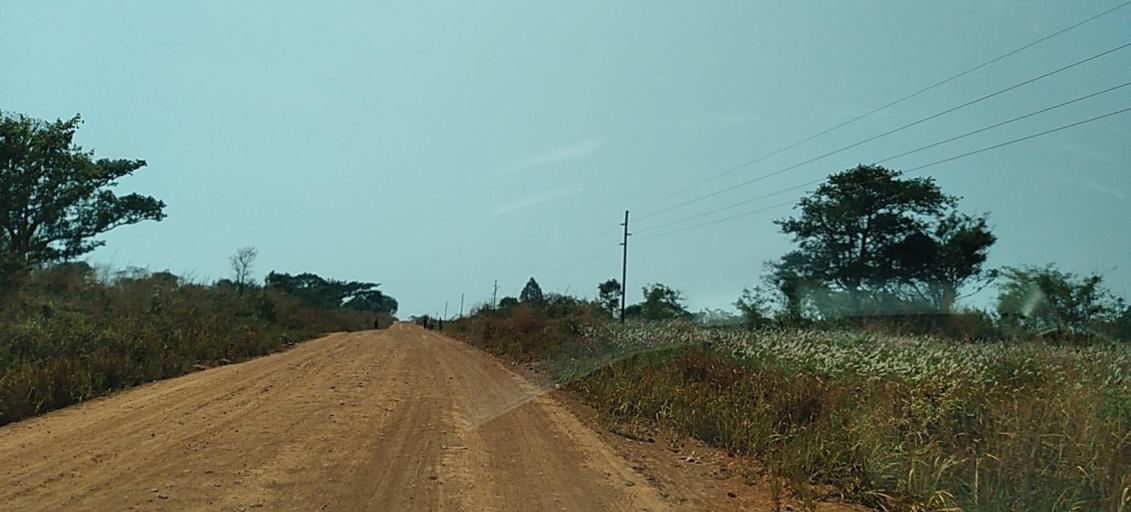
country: ZM
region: North-Western
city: Kansanshi
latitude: -12.0064
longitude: 26.5732
